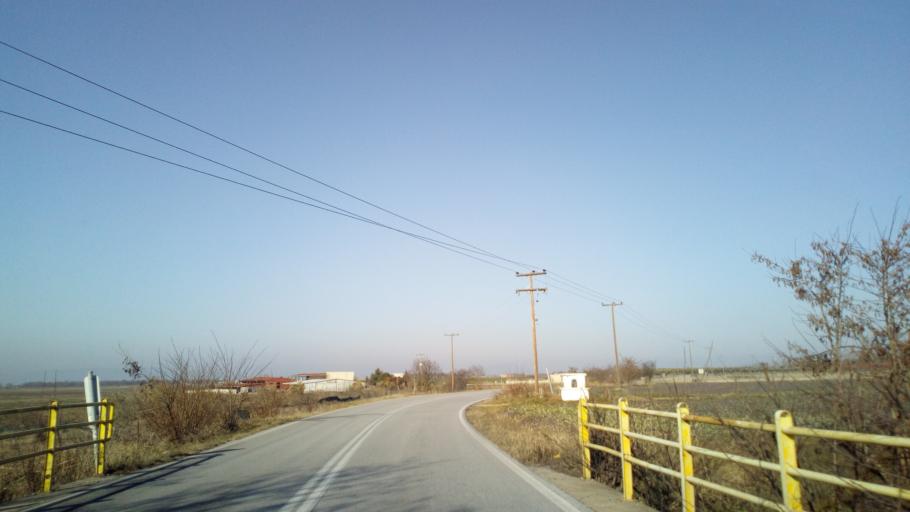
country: GR
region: Central Macedonia
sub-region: Nomos Thessalonikis
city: Kolchikon
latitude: 40.7387
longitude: 23.1455
